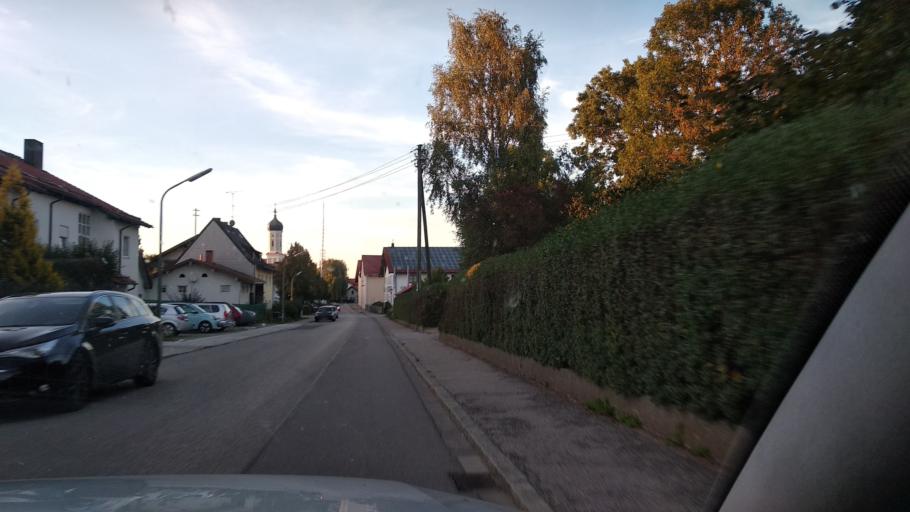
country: DE
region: Bavaria
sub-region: Upper Bavaria
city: Zorneding
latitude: 48.0806
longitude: 11.8247
